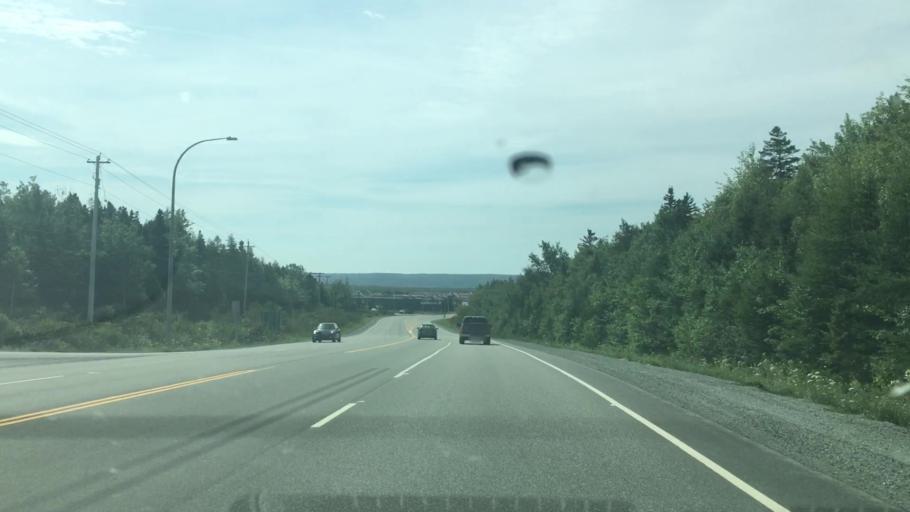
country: CA
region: Nova Scotia
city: Port Hawkesbury
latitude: 45.6243
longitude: -61.3329
